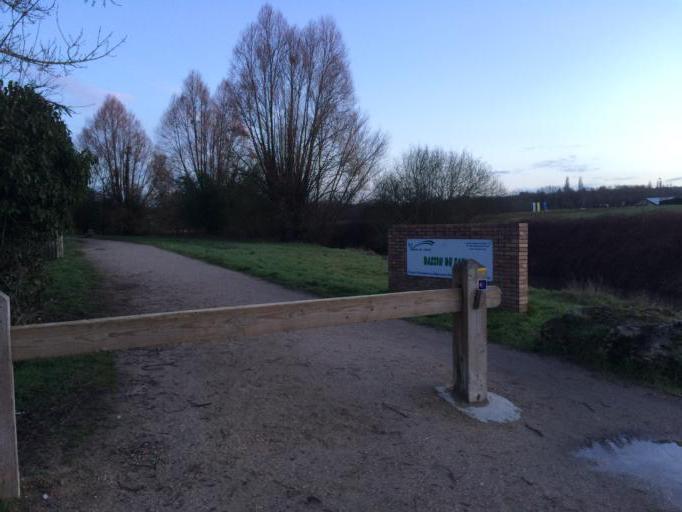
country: FR
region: Ile-de-France
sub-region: Departement de l'Essonne
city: Saulx-les-Chartreux
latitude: 48.6999
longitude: 2.2700
